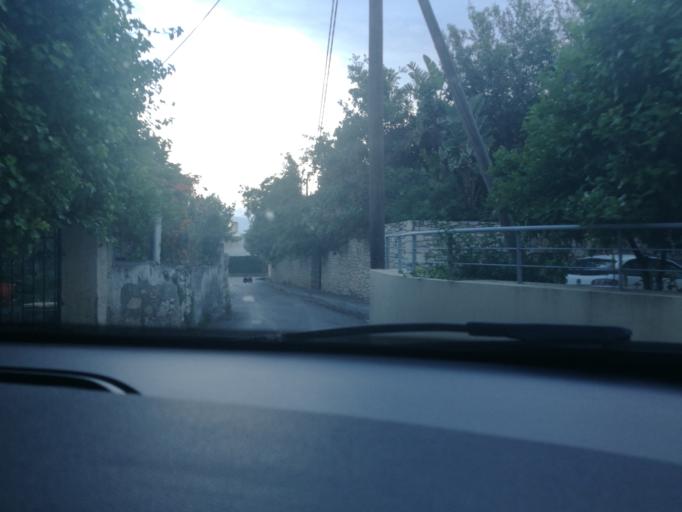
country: GR
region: Crete
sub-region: Nomos Irakleiou
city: Irakleion
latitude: 35.3166
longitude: 25.1485
